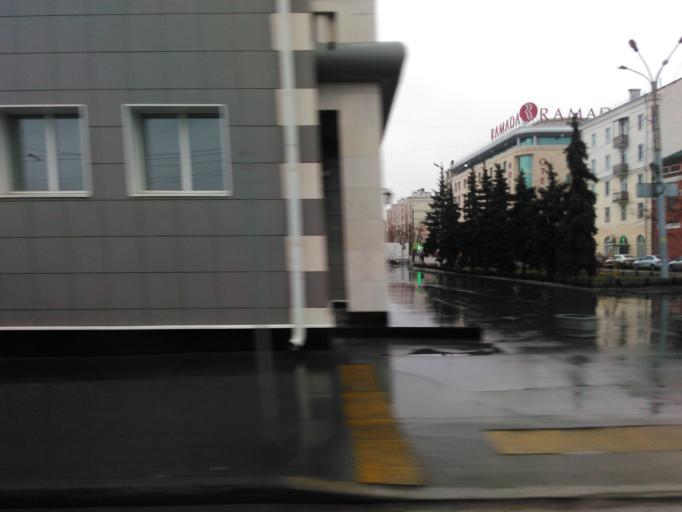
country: RU
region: Tatarstan
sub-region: Gorod Kazan'
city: Kazan
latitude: 55.7883
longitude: 49.1028
